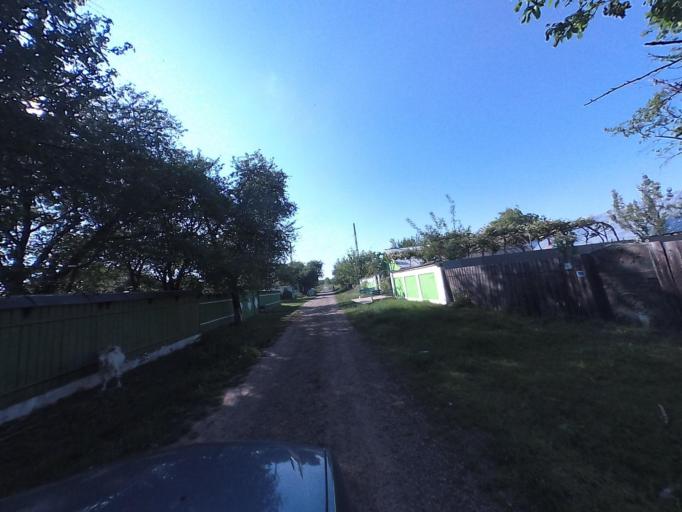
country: RO
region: Neamt
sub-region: Comuna Dulcesti
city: Dulcesti
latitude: 46.9972
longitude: 26.7826
